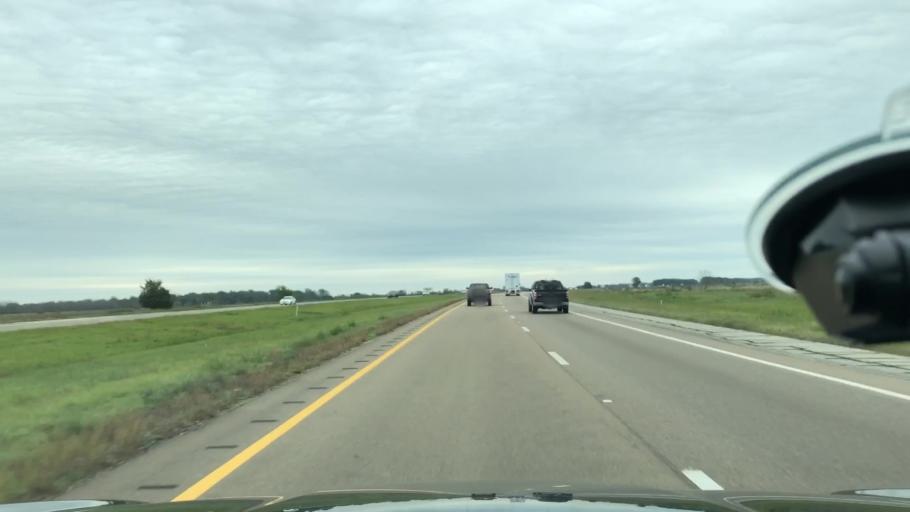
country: US
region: Texas
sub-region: Morris County
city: Omaha
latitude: 33.2873
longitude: -94.7855
